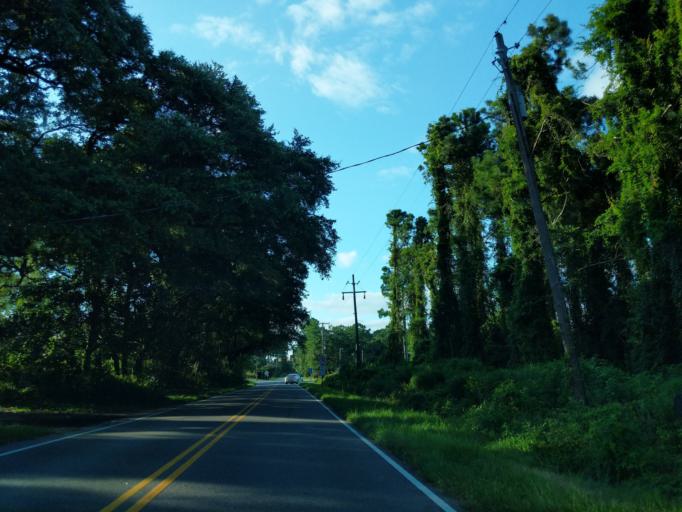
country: US
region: South Carolina
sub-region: Charleston County
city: Awendaw
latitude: 33.0940
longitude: -79.4756
